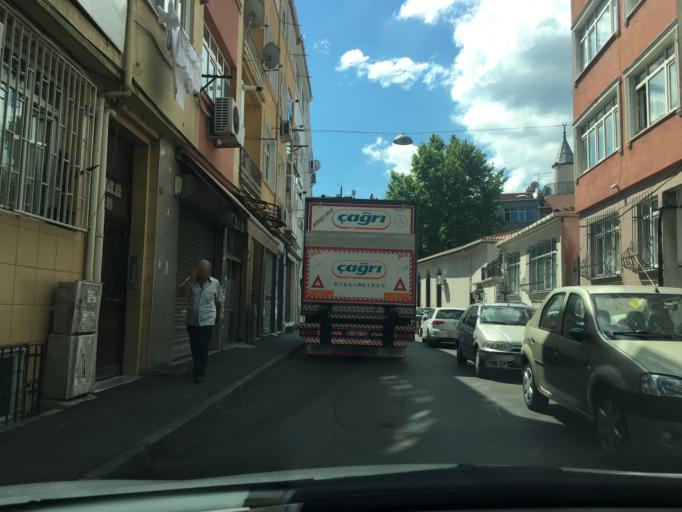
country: TR
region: Istanbul
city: Istanbul
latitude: 41.0123
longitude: 28.9276
